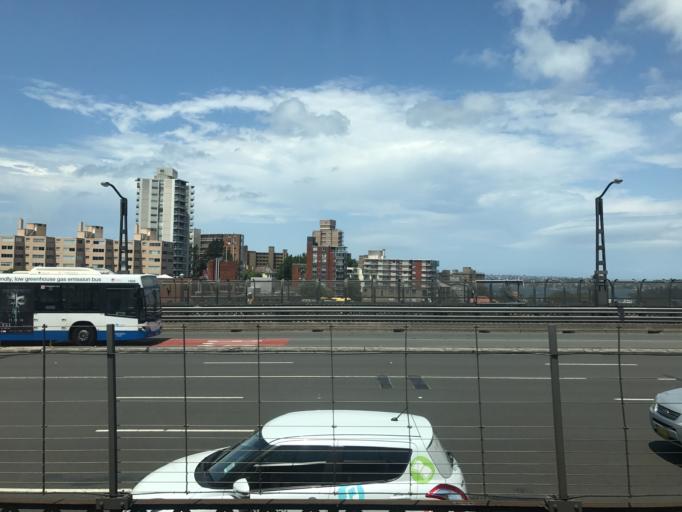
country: AU
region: New South Wales
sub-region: North Sydney
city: Milsons Point
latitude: -33.8487
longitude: 151.2126
